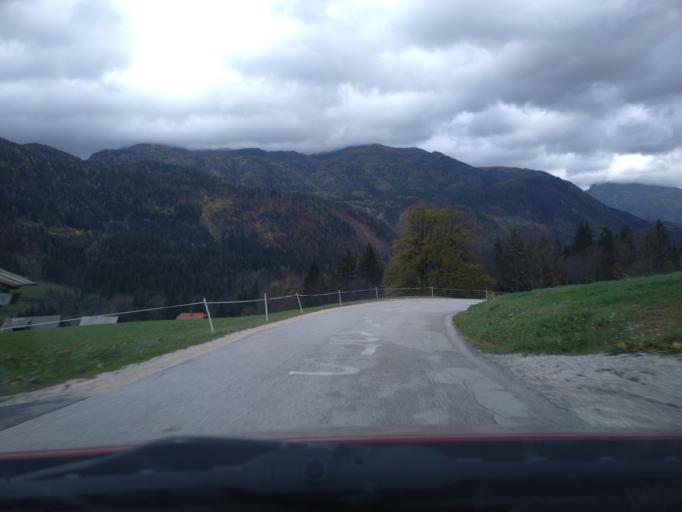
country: SI
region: Luce
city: Luce
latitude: 46.2979
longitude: 14.6994
